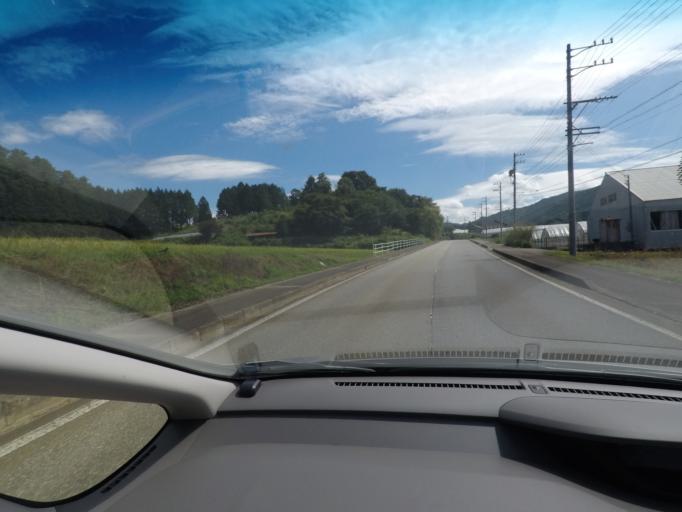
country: JP
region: Gifu
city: Takayama
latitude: 36.1383
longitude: 137.2871
